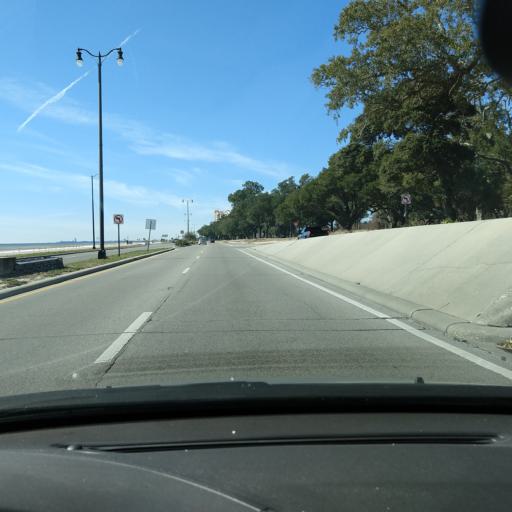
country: US
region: Mississippi
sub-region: Harrison County
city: Gulfport
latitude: 30.3837
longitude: -89.0212
